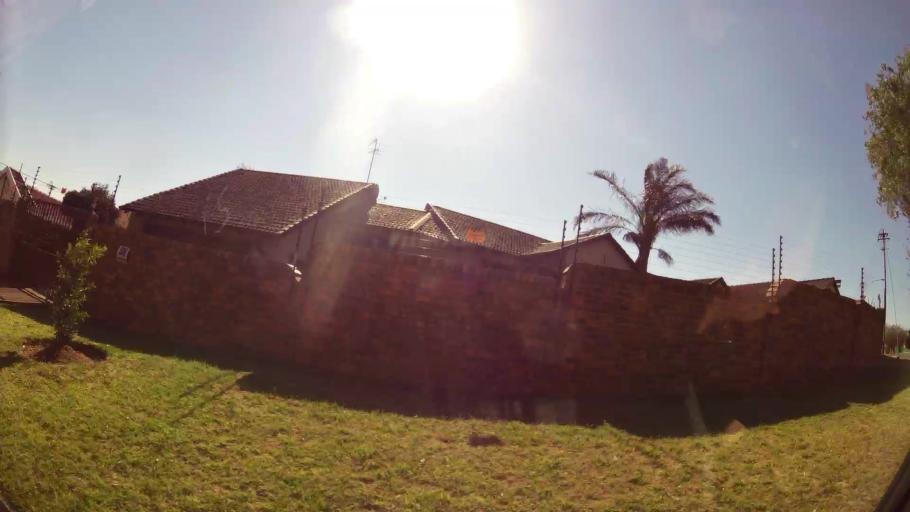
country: ZA
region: Gauteng
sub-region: City of Johannesburg Metropolitan Municipality
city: Johannesburg
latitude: -26.2686
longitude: 28.0272
